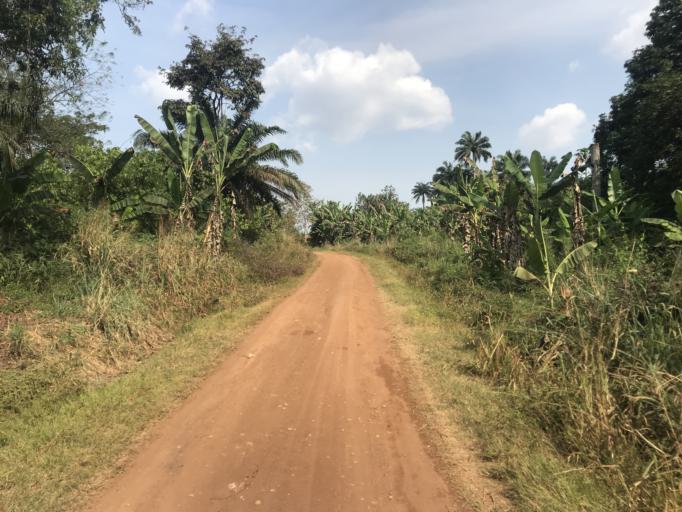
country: NG
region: Osun
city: Osu
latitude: 7.6470
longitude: 4.6601
